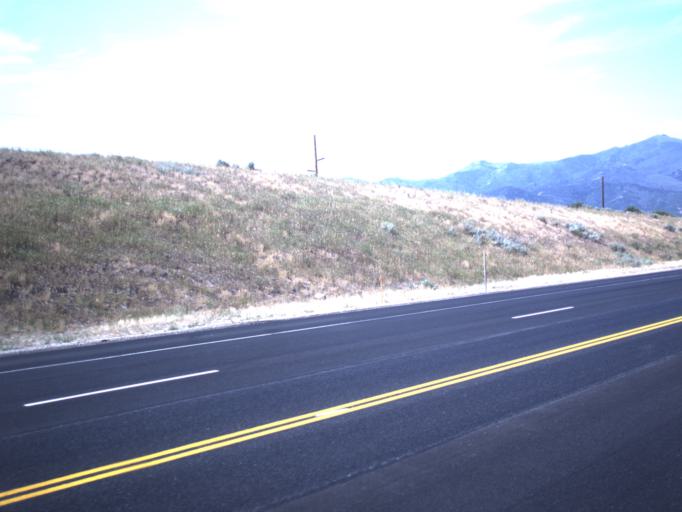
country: US
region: Utah
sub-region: Summit County
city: Kamas
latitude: 40.6340
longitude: -111.3799
